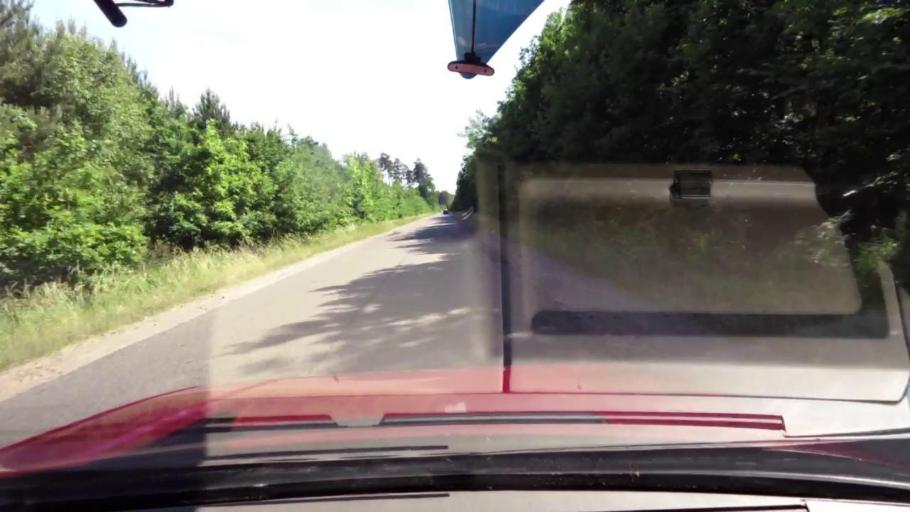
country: PL
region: Pomeranian Voivodeship
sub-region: Powiat slupski
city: Kepice
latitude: 54.3254
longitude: 16.9621
